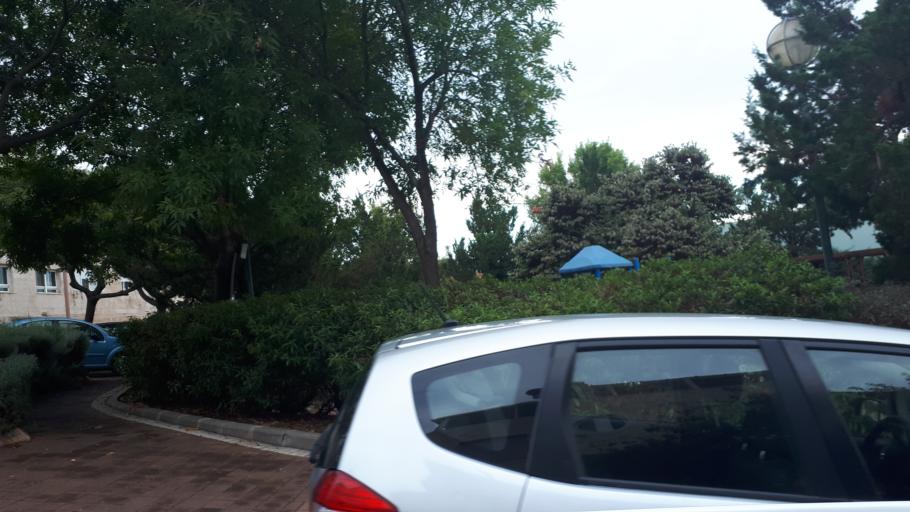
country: IL
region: Central District
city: Modiin
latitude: 31.9079
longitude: 35.0092
